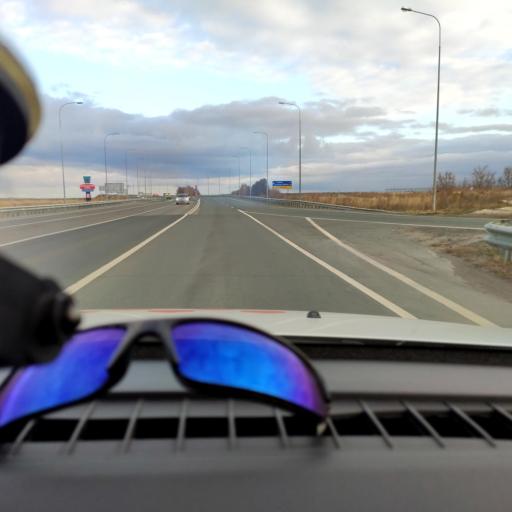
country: RU
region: Samara
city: Bereza
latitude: 53.4930
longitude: 50.1178
